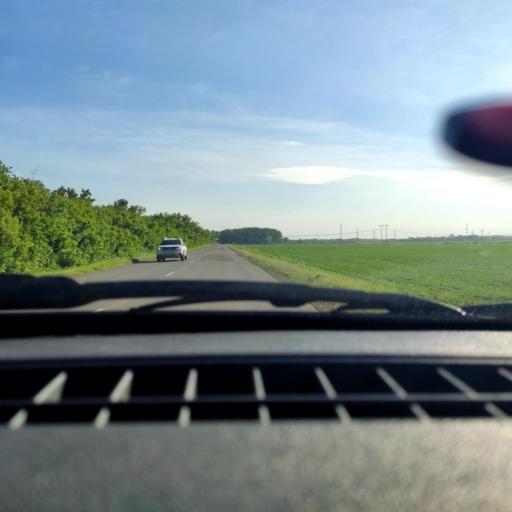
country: RU
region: Bashkortostan
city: Avdon
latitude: 54.4375
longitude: 55.8330
